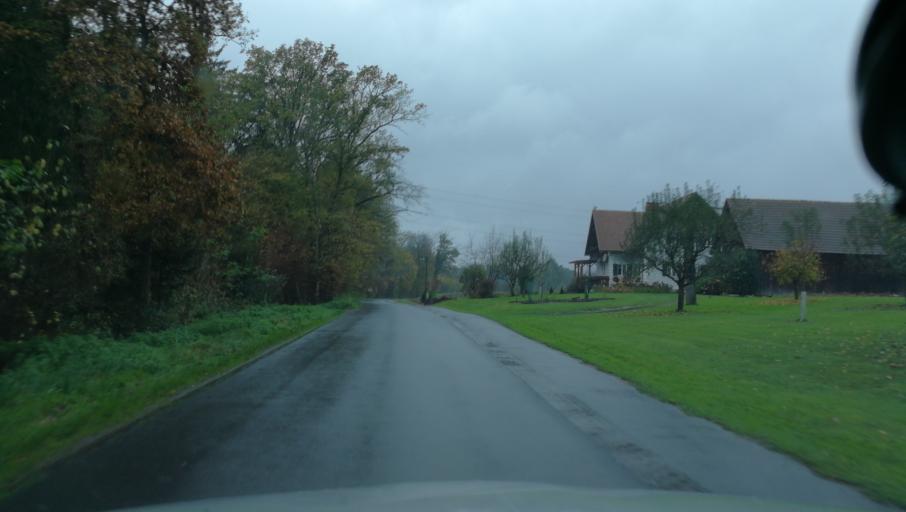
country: AT
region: Styria
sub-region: Politischer Bezirk Leibnitz
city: Strass in Steiermark
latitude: 46.7358
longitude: 15.6526
